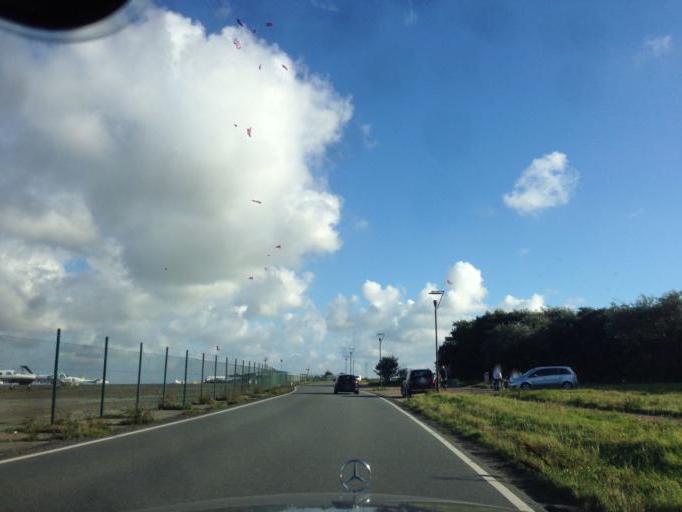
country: DE
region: Schleswig-Holstein
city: Tinnum
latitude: 54.9130
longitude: 8.3243
